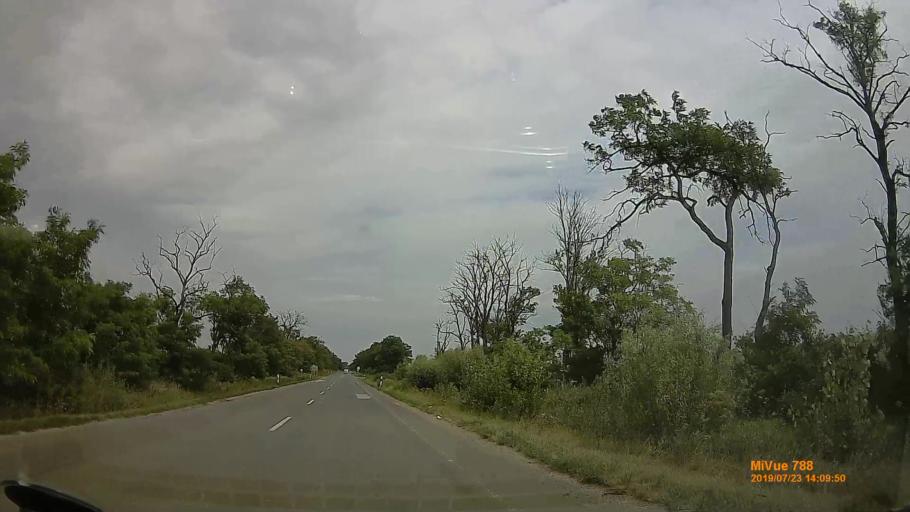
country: HU
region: Szabolcs-Szatmar-Bereg
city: Tiszavasvari
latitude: 47.9583
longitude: 21.4046
